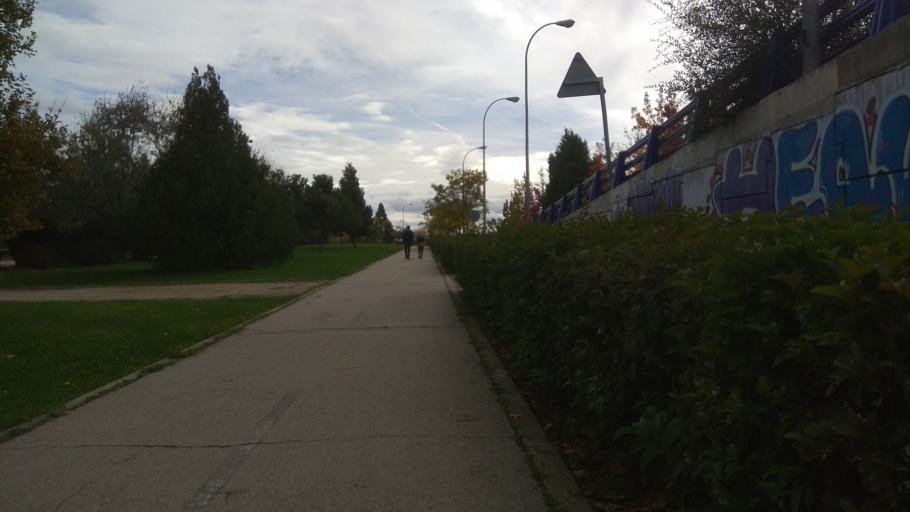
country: ES
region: Madrid
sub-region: Provincia de Madrid
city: Vicalvaro
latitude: 40.4109
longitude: -3.6182
